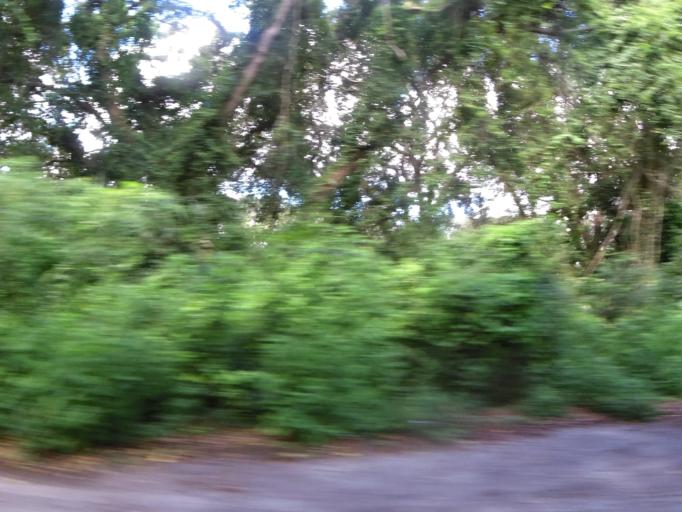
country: US
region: Florida
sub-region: Nassau County
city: Fernandina Beach
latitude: 30.5960
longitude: -81.4473
